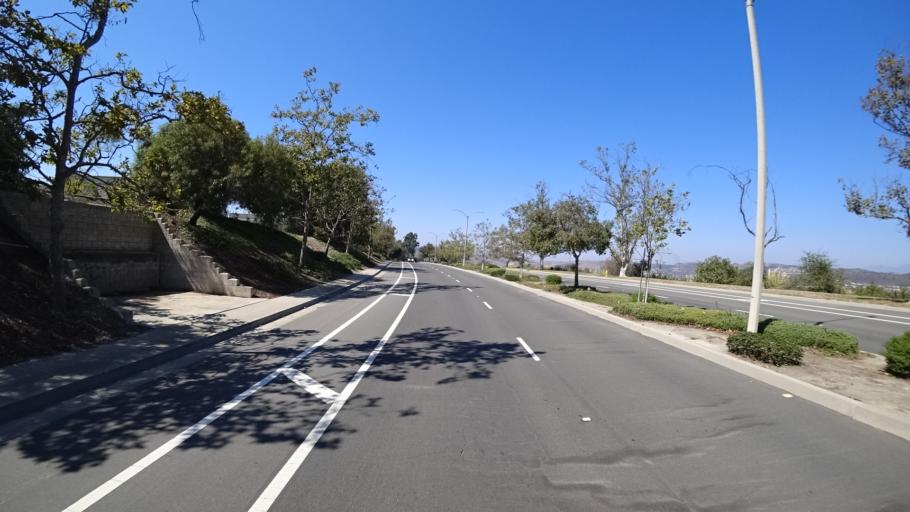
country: US
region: California
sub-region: Orange County
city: San Clemente
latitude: 33.4495
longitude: -117.5890
